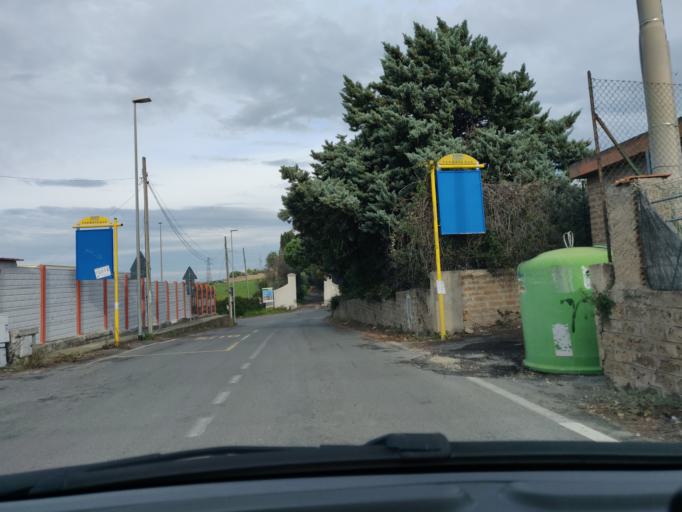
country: IT
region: Latium
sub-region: Citta metropolitana di Roma Capitale
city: Civitavecchia
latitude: 42.1040
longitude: 11.8120
